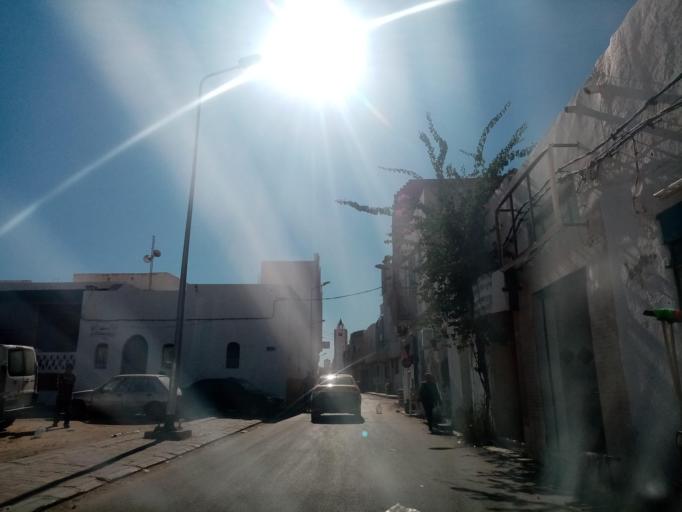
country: TN
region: Qabis
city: Gabes
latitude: 33.8812
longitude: 10.0892
